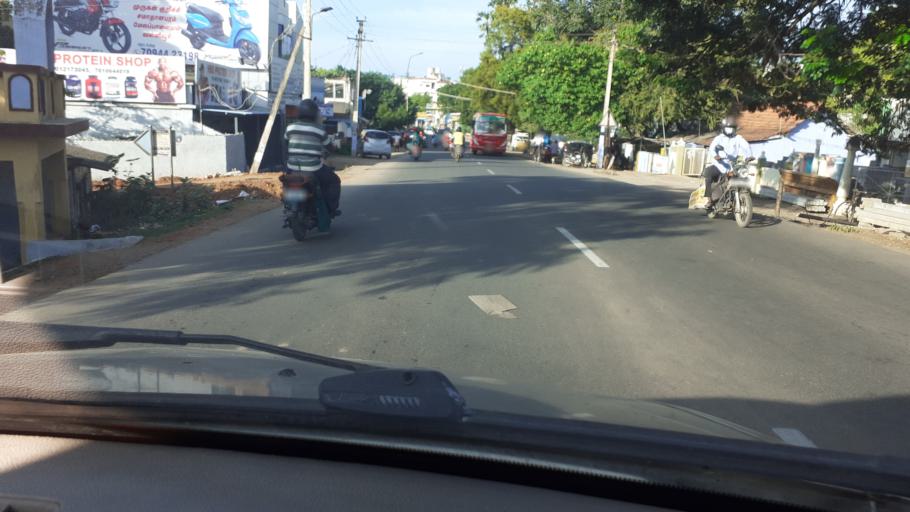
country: IN
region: Tamil Nadu
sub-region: Tirunelveli Kattabo
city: Tirunelveli
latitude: 8.7117
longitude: 77.7315
